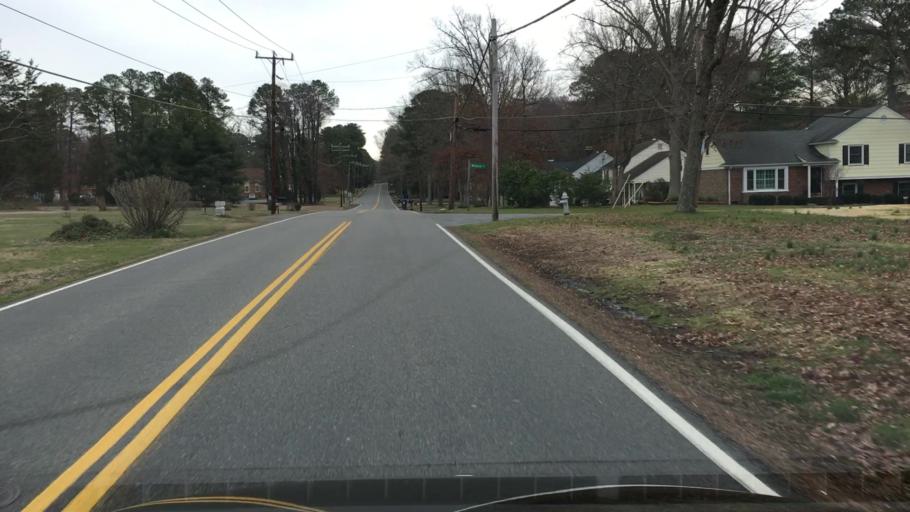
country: US
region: Virginia
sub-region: Henrico County
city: Tuckahoe
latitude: 37.5883
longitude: -77.5807
